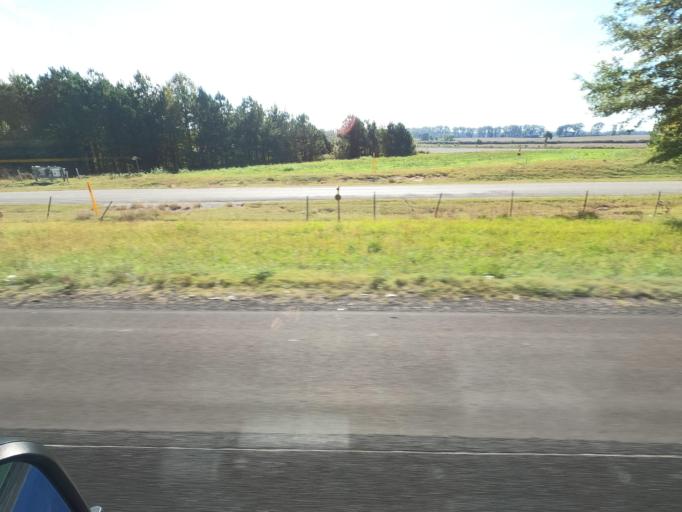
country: US
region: Tennessee
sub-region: Tipton County
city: Mason
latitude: 35.3367
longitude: -89.5448
